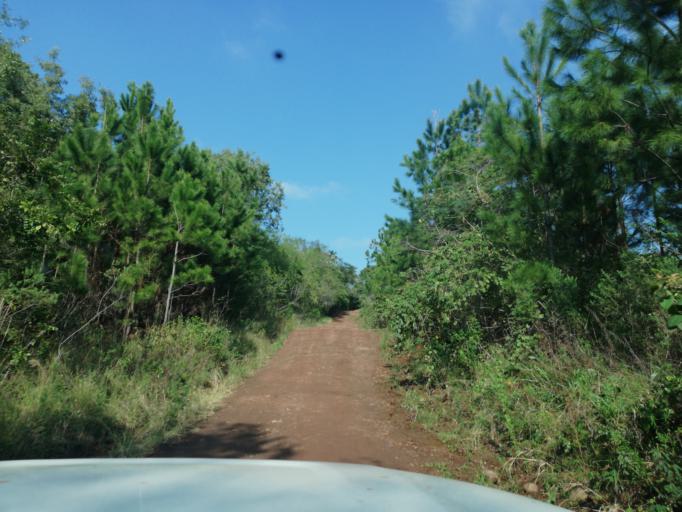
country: AR
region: Misiones
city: Cerro Azul
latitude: -27.6175
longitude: -55.5230
